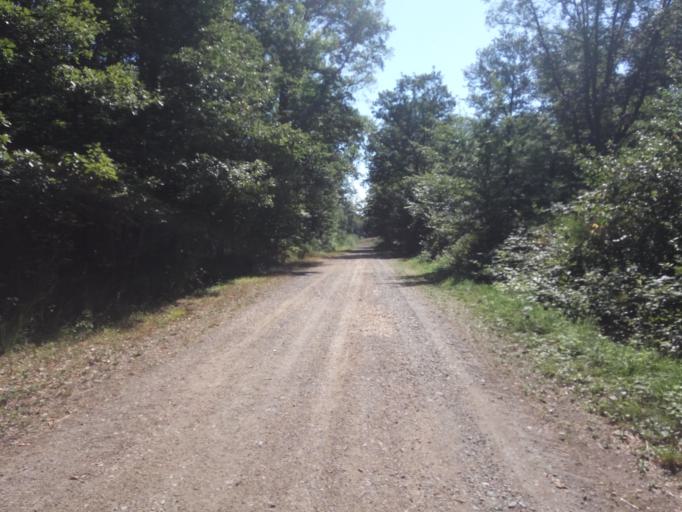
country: FR
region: Auvergne
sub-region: Departement de l'Allier
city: Brugheas
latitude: 46.0880
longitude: 3.3495
